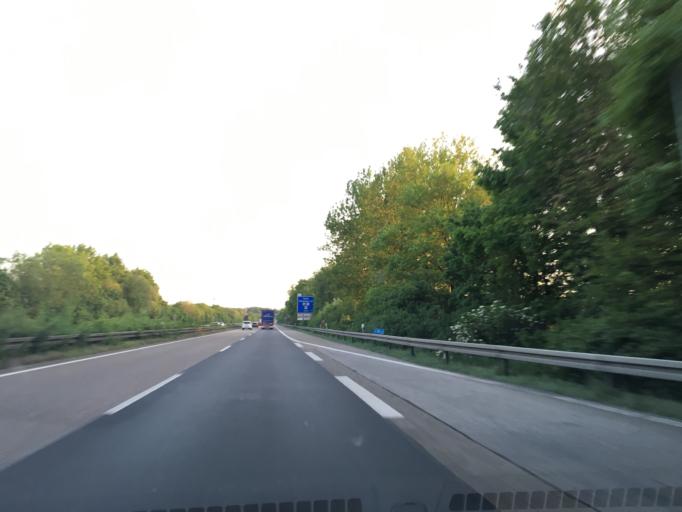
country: DE
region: North Rhine-Westphalia
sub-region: Regierungsbezirk Munster
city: Lotte
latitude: 52.2630
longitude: 7.9232
